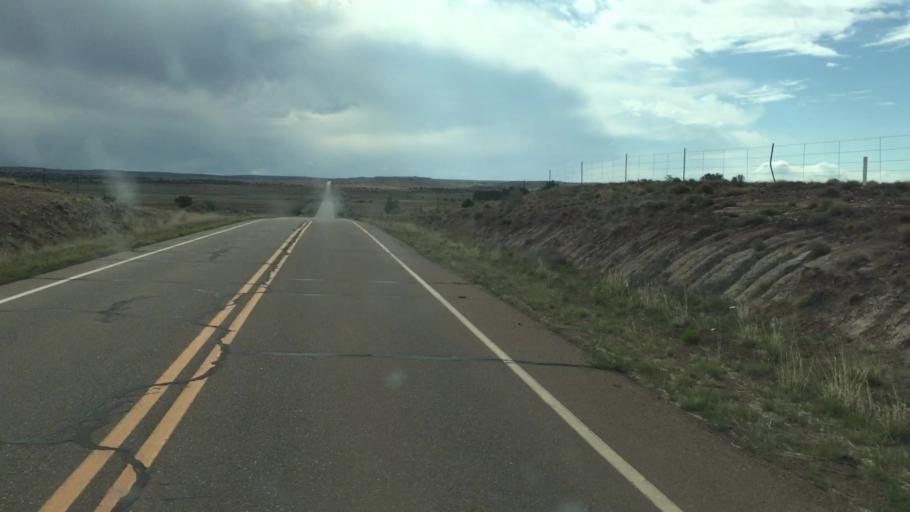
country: US
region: Arizona
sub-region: Apache County
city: Saint Johns
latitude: 34.5106
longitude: -109.6853
